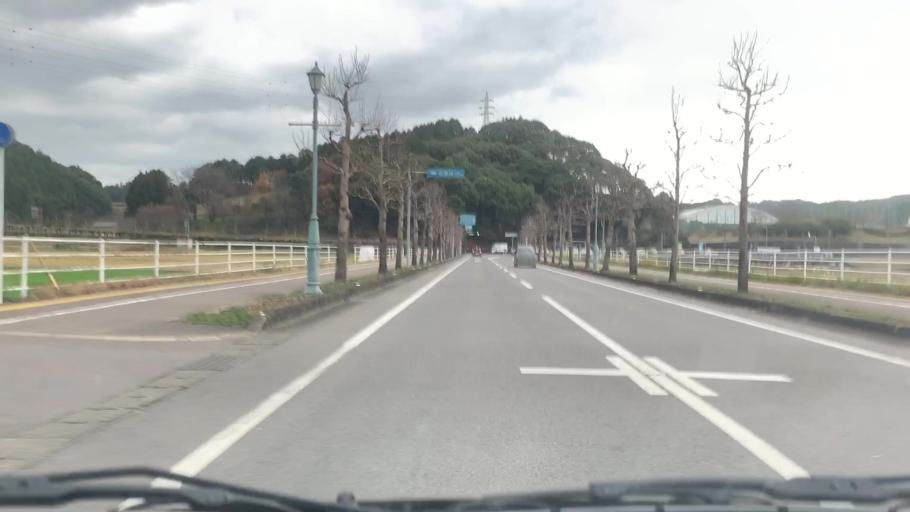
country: JP
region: Saga Prefecture
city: Ureshinomachi-shimojuku
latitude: 33.1063
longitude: 129.9849
